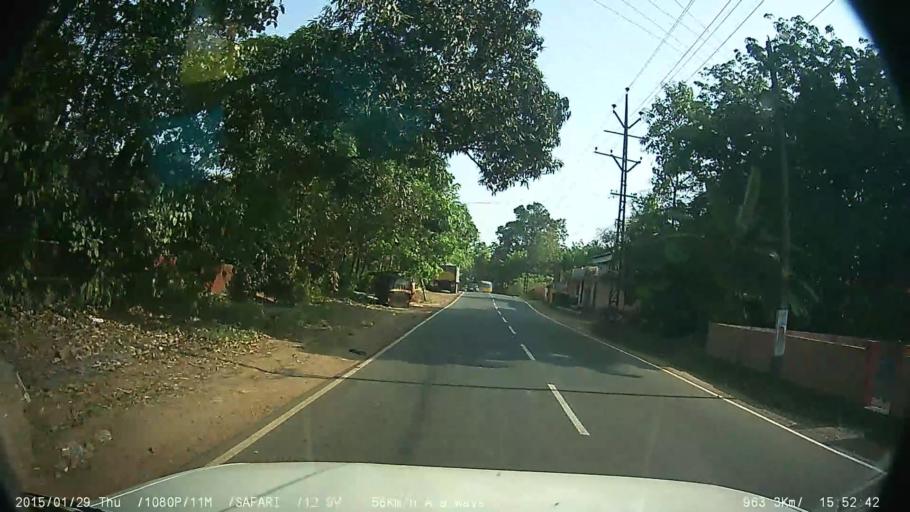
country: IN
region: Kerala
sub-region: Kottayam
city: Changanacheri
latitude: 9.4863
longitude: 76.5720
